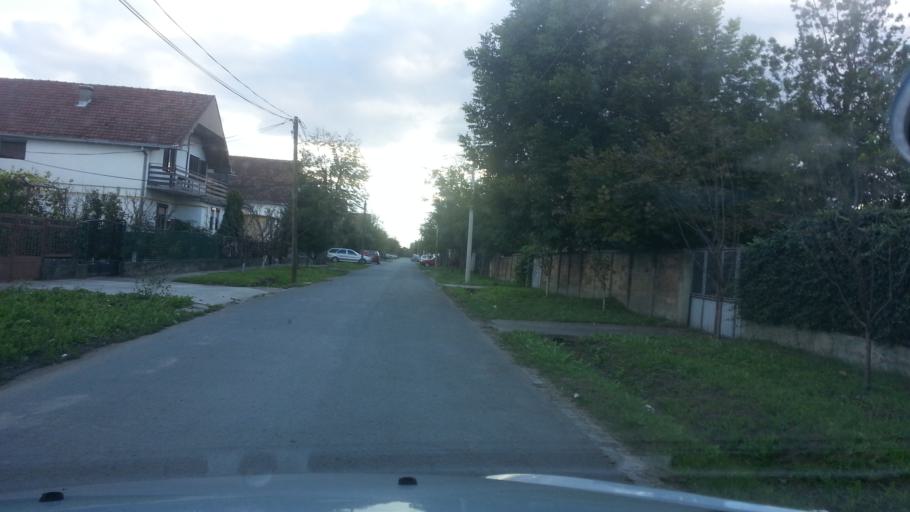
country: RS
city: Novi Banovci
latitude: 44.9057
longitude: 20.2695
